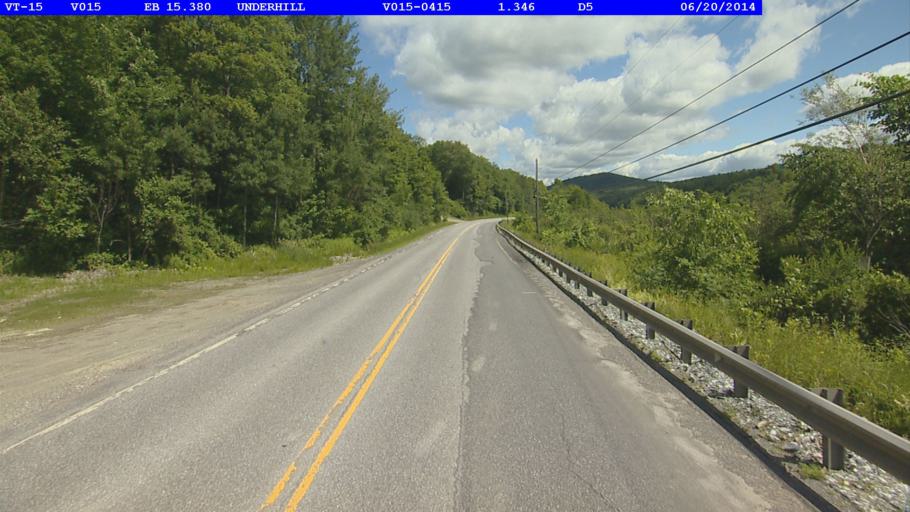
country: US
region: Vermont
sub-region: Chittenden County
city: Jericho
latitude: 44.5438
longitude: -72.9487
